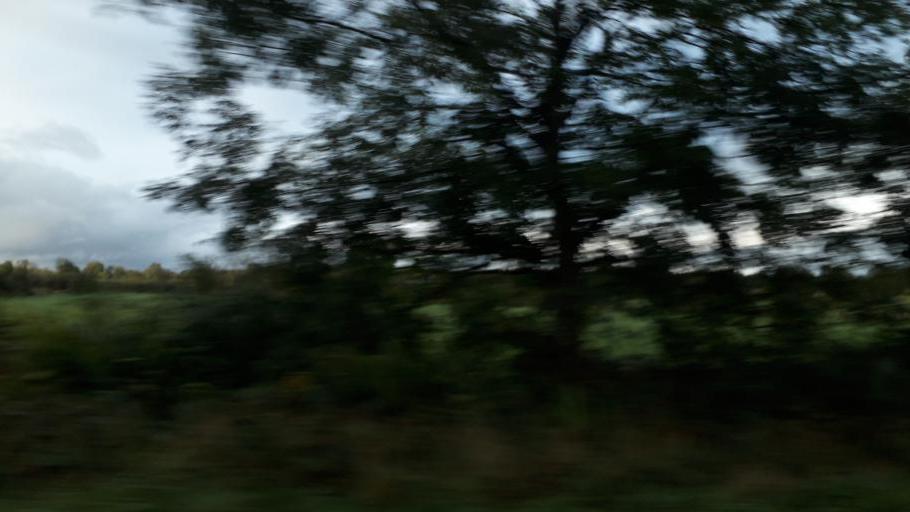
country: IE
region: Leinster
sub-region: An Longfort
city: Lanesborough
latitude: 53.7478
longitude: -7.9435
